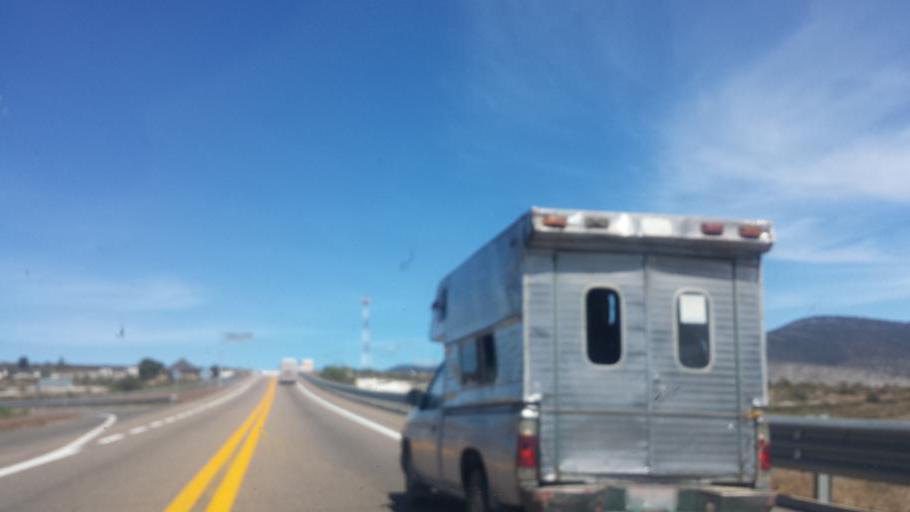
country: MX
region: Oaxaca
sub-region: Villa Tejupam de la Union
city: Villa Tejupam de la Union
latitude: 17.8876
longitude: -97.3723
